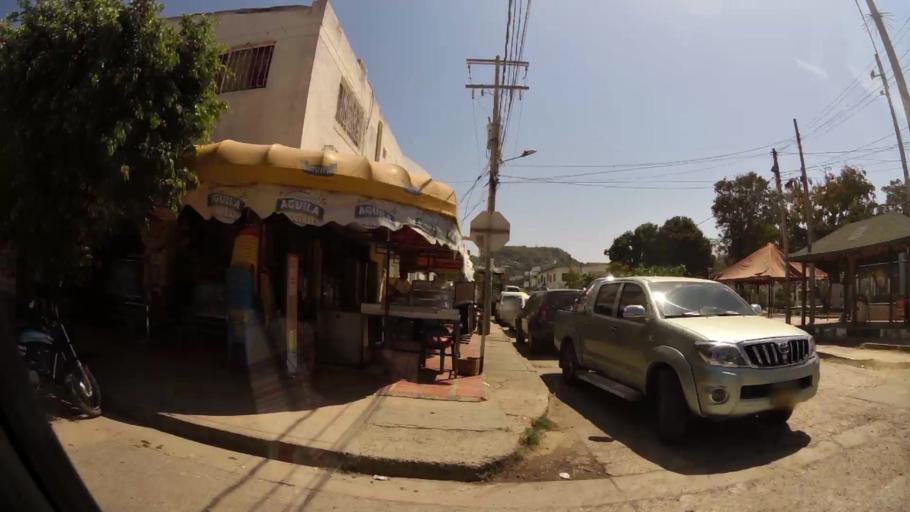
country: CO
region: Bolivar
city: Cartagena
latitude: 10.4312
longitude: -75.5338
